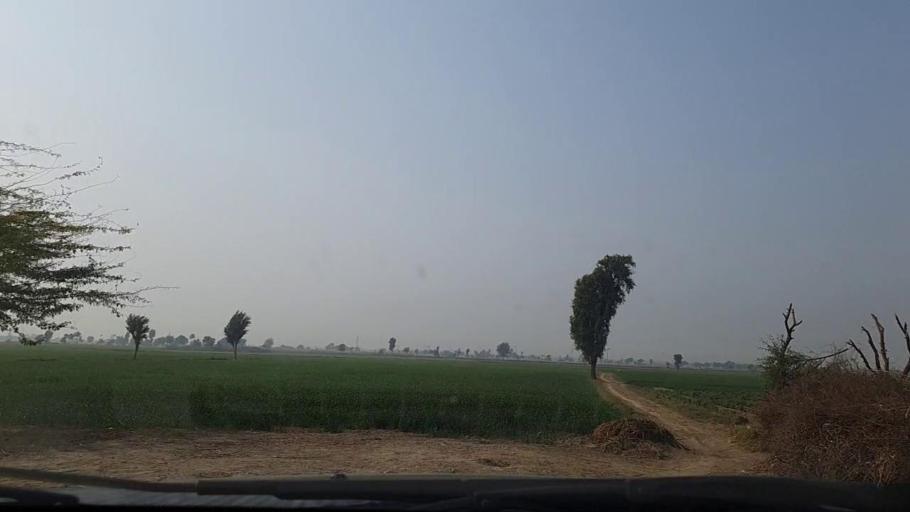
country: PK
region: Sindh
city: Sanghar
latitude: 26.0444
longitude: 68.9770
